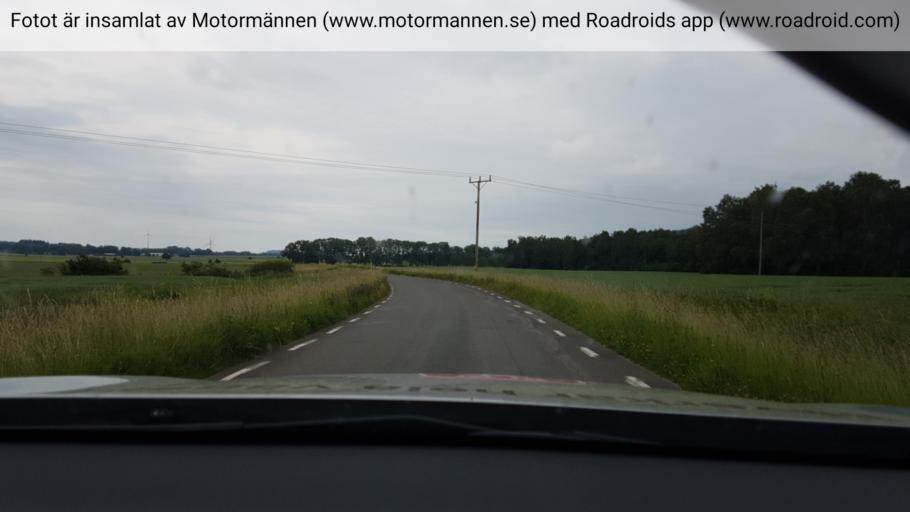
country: SE
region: Vaestra Goetaland
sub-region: Tidaholms Kommun
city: Tidaholm
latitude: 58.1884
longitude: 13.8253
